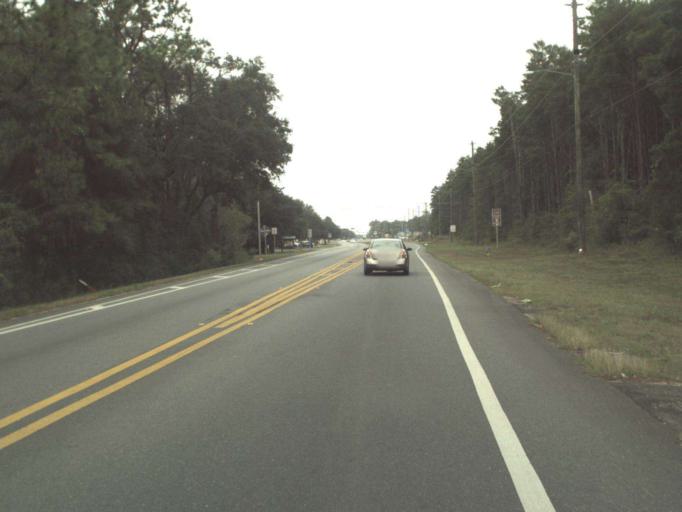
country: US
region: Florida
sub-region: Leon County
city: Woodville
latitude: 30.3696
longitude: -84.2674
